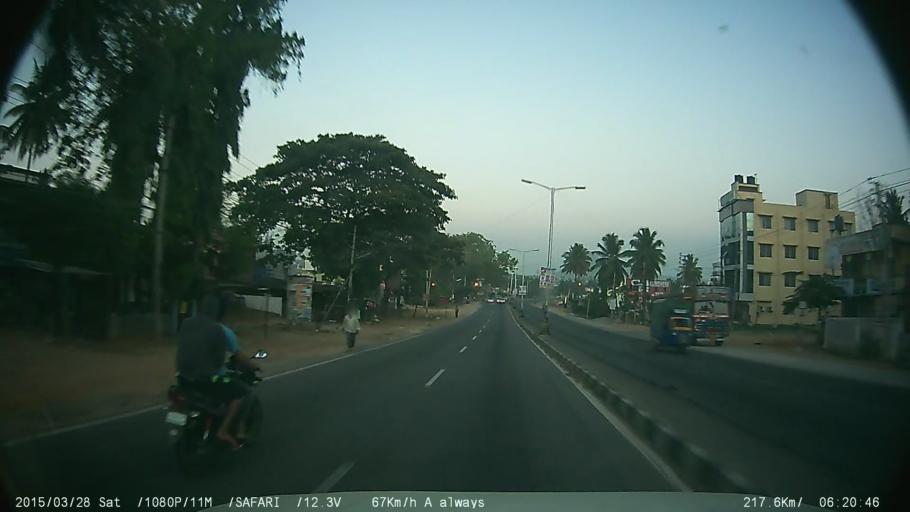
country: IN
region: Karnataka
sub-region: Ramanagara
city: Ramanagaram
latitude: 12.7290
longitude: 77.2855
